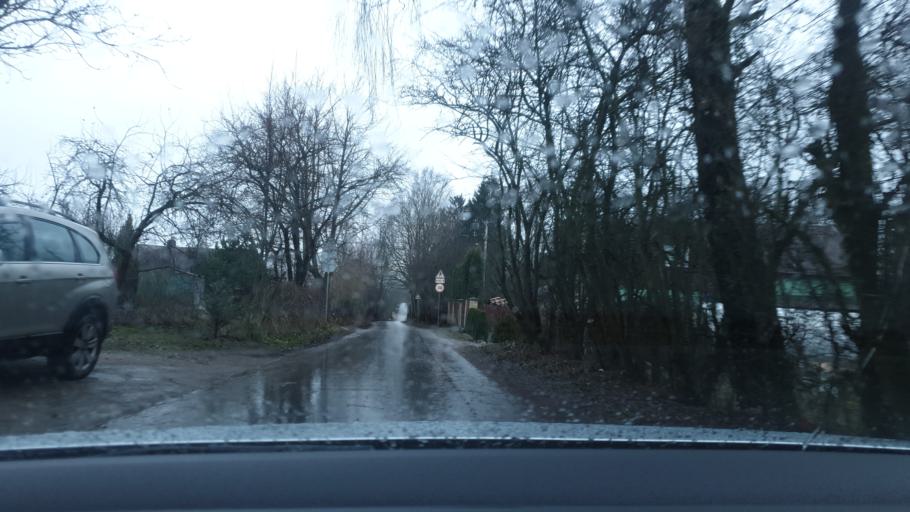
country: LT
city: Skaidiskes
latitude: 54.7051
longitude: 25.4088
